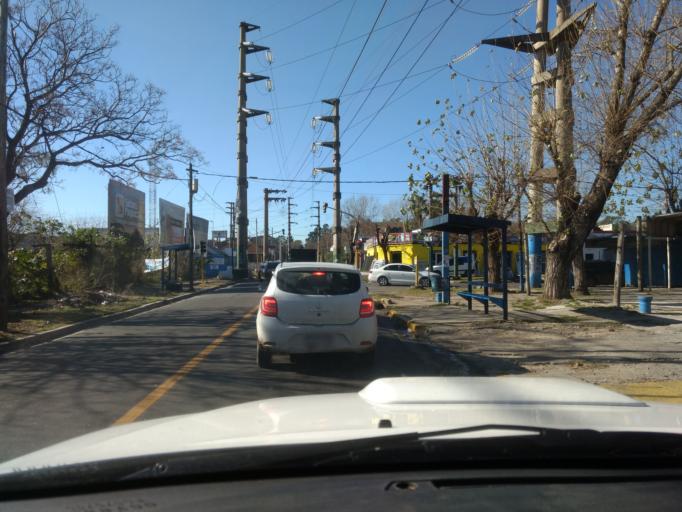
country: AR
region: Buenos Aires
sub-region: Partido de Lomas de Zamora
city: Lomas de Zamora
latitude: -34.7814
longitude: -58.4241
